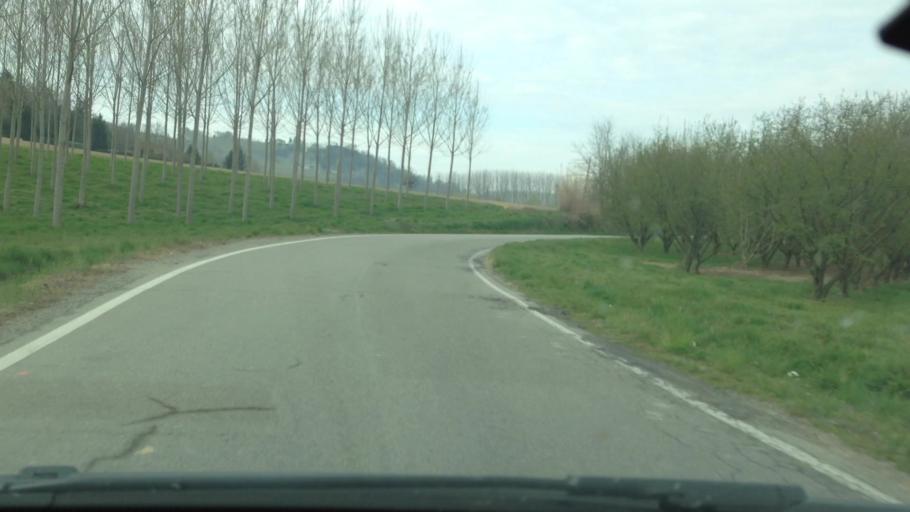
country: IT
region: Piedmont
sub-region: Provincia di Asti
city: Revigliasco d'Asti
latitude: 44.8941
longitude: 8.1573
